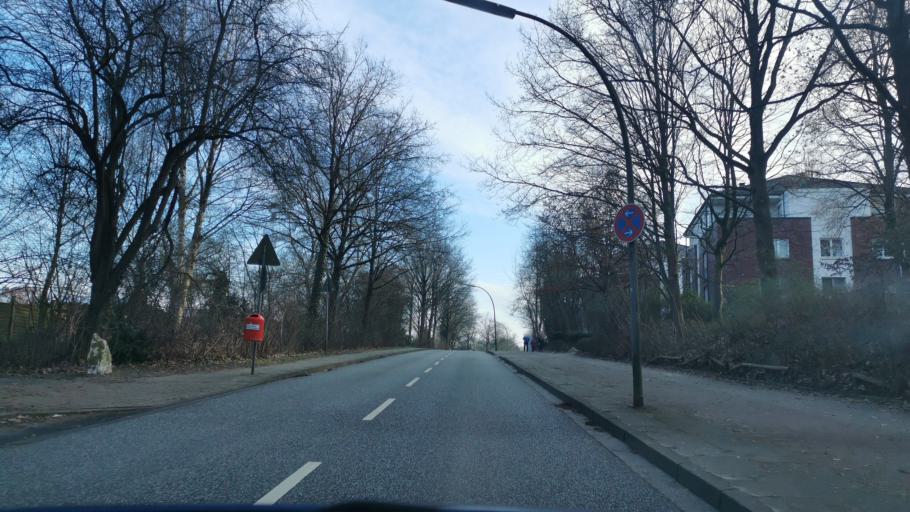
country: DE
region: Lower Saxony
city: Seevetal
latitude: 53.4291
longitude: 9.9726
